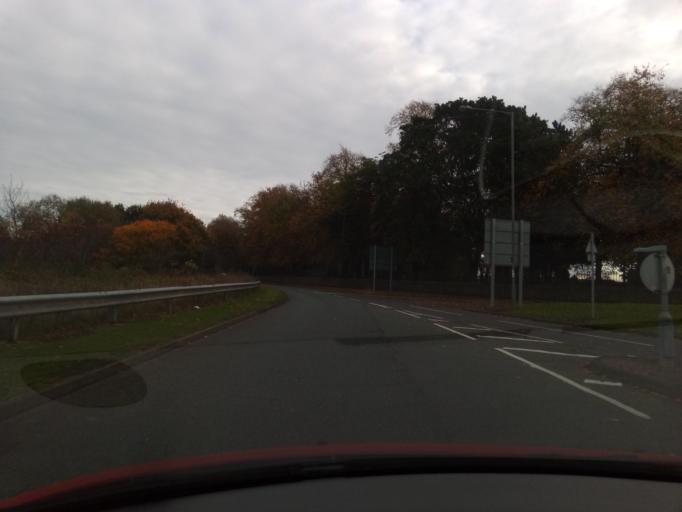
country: GB
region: England
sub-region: County Durham
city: Bishop Auckland
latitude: 54.6529
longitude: -1.6667
